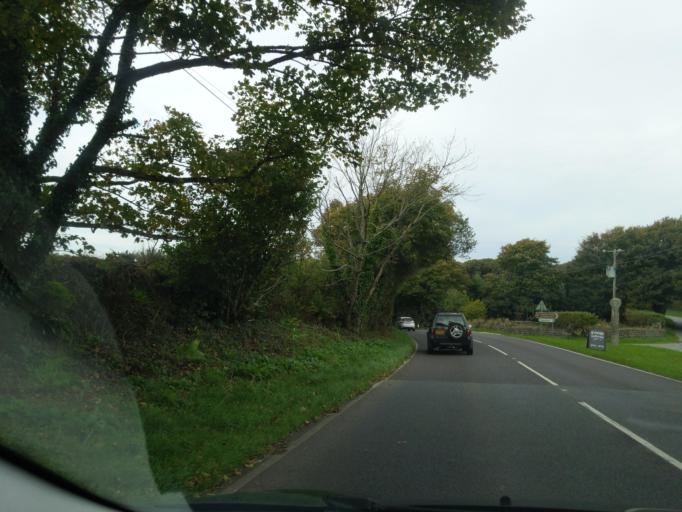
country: GB
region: England
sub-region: Cornwall
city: Bodmin
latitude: 50.4944
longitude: -4.7682
